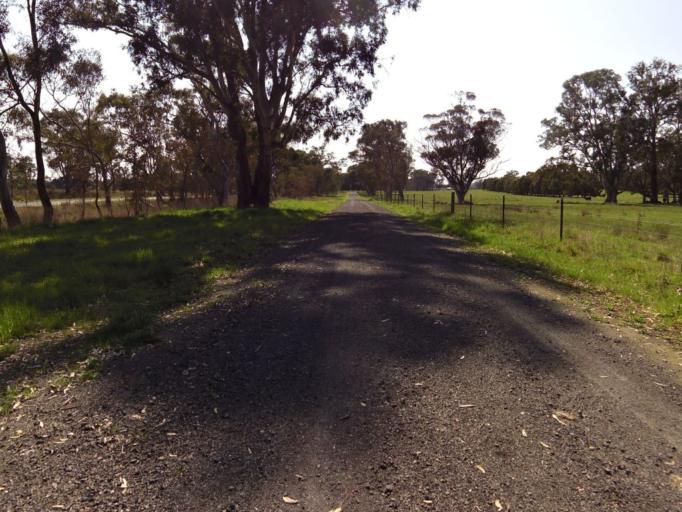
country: AU
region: Victoria
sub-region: Murrindindi
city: Alexandra
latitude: -37.1148
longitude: 145.6070
